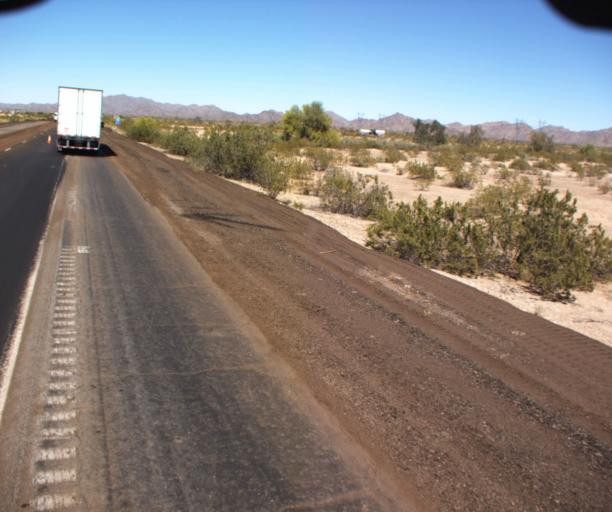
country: US
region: Arizona
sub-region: Maricopa County
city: Gila Bend
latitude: 33.0417
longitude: -112.6446
